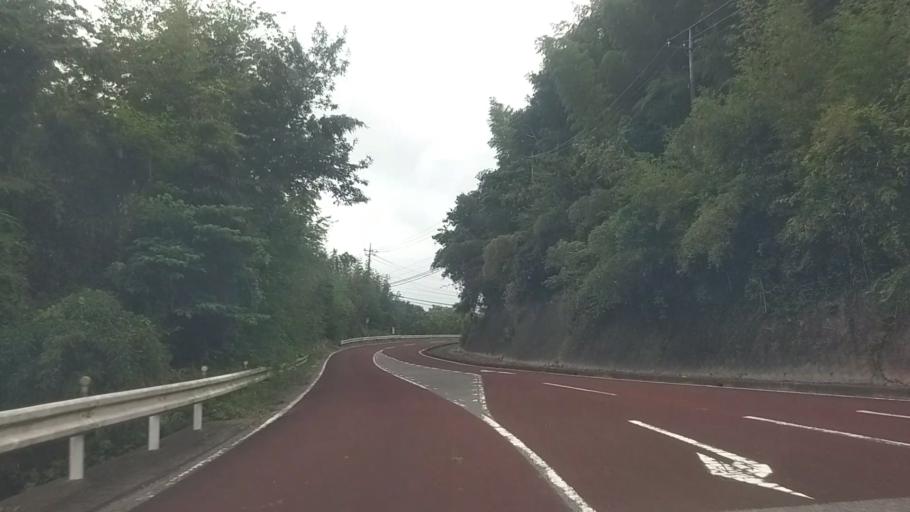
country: JP
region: Chiba
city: Kawaguchi
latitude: 35.2288
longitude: 140.0812
